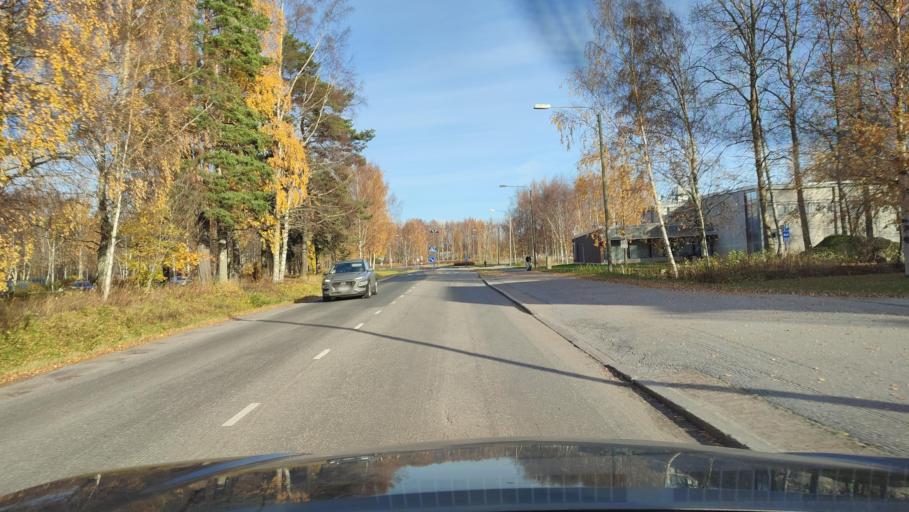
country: FI
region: Ostrobothnia
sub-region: Vaasa
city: Vaasa
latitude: 63.0867
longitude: 21.6449
